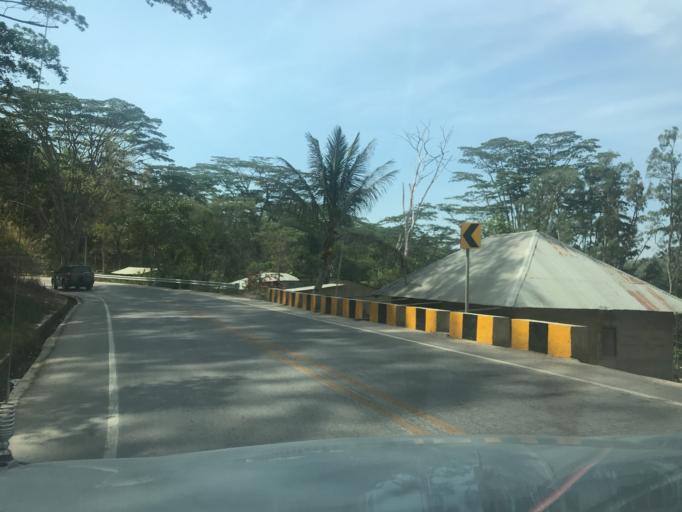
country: TL
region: Aileu
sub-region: Aileu Villa
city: Aileu
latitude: -8.6782
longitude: 125.5507
